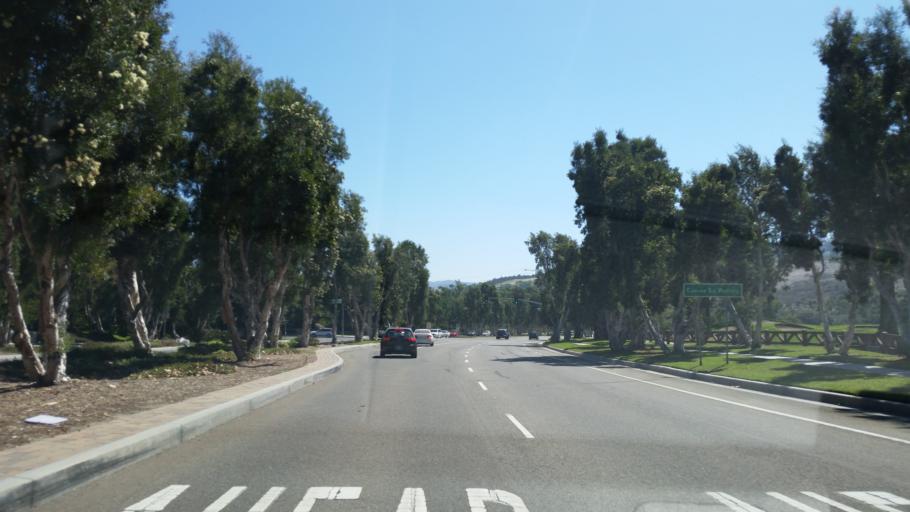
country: US
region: California
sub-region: Orange County
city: San Clemente
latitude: 33.4623
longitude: -117.5935
